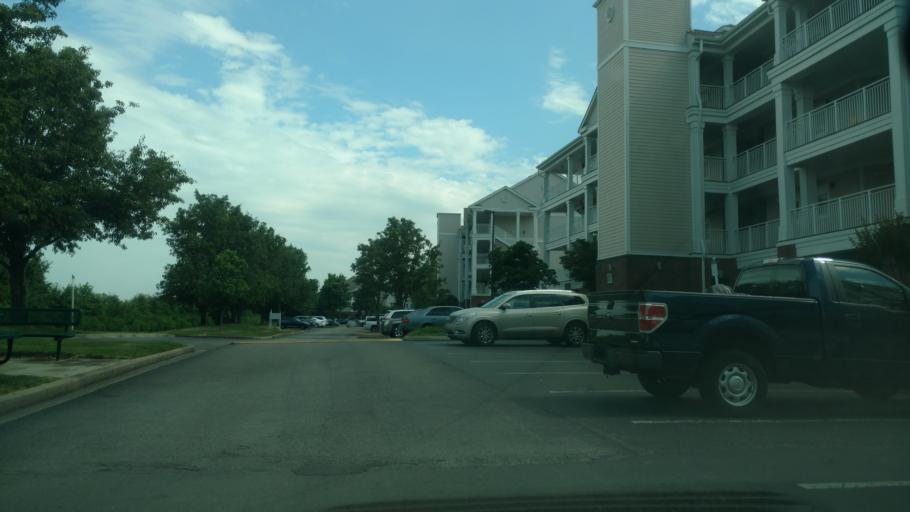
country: US
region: Tennessee
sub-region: Davidson County
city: Lakewood
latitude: 36.2214
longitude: -86.7049
